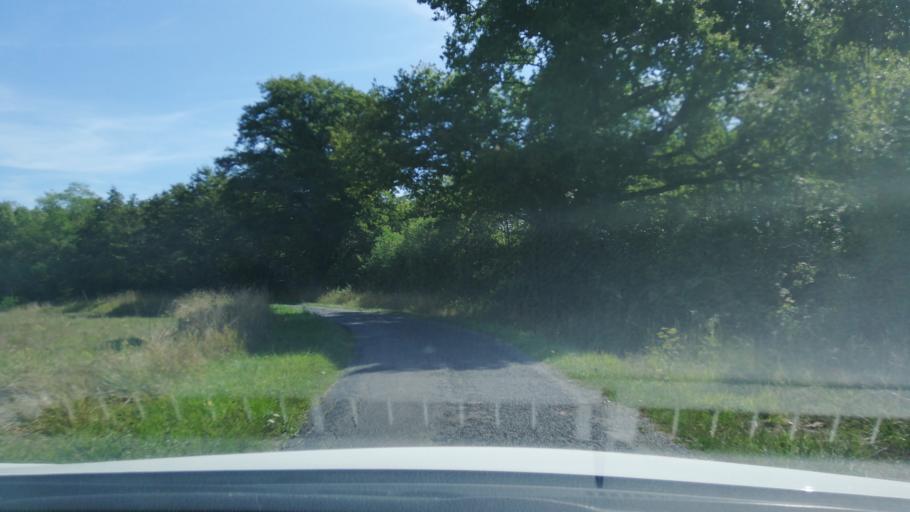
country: FR
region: Centre
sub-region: Departement d'Indre-et-Loire
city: Mazieres-de-Touraine
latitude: 47.3909
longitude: 0.4396
